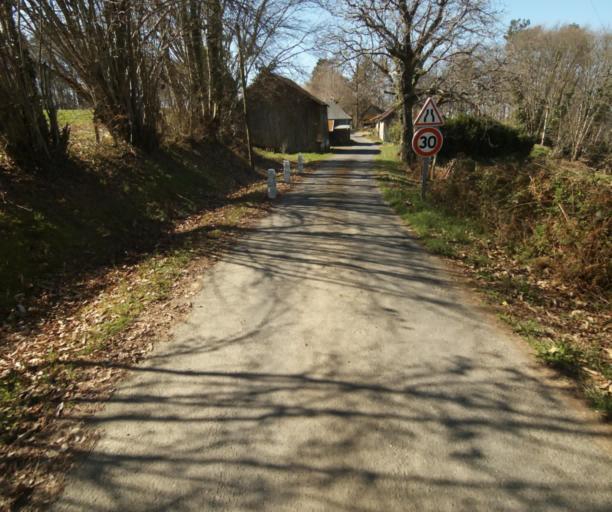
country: FR
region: Limousin
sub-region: Departement de la Correze
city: Saint-Mexant
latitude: 45.3114
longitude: 1.6105
